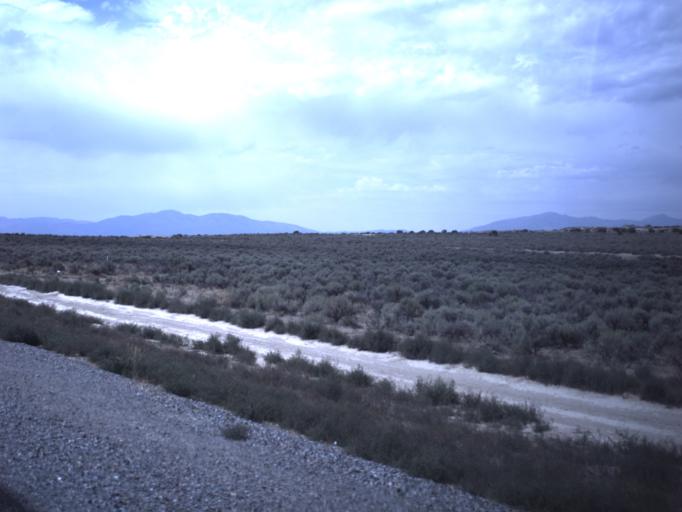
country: US
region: Utah
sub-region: Utah County
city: Eagle Mountain
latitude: 40.2330
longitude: -112.1735
